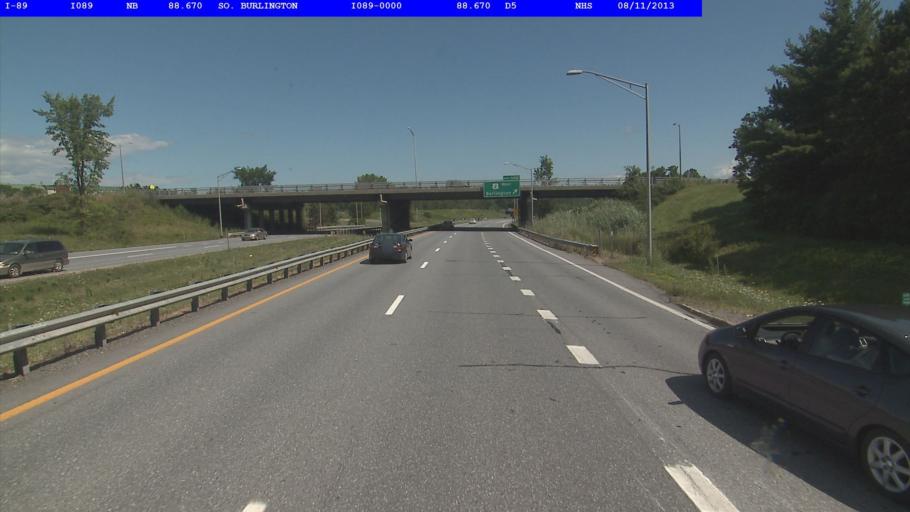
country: US
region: Vermont
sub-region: Chittenden County
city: South Burlington
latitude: 44.4692
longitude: -73.1846
